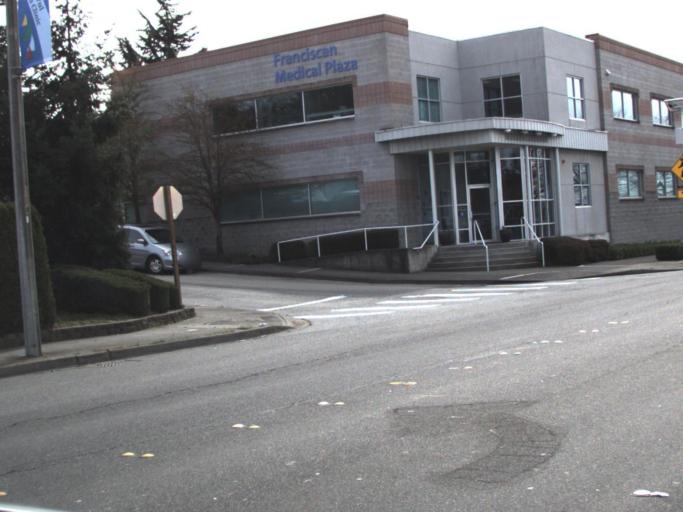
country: US
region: Washington
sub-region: King County
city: Des Moines
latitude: 47.4046
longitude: -122.3247
